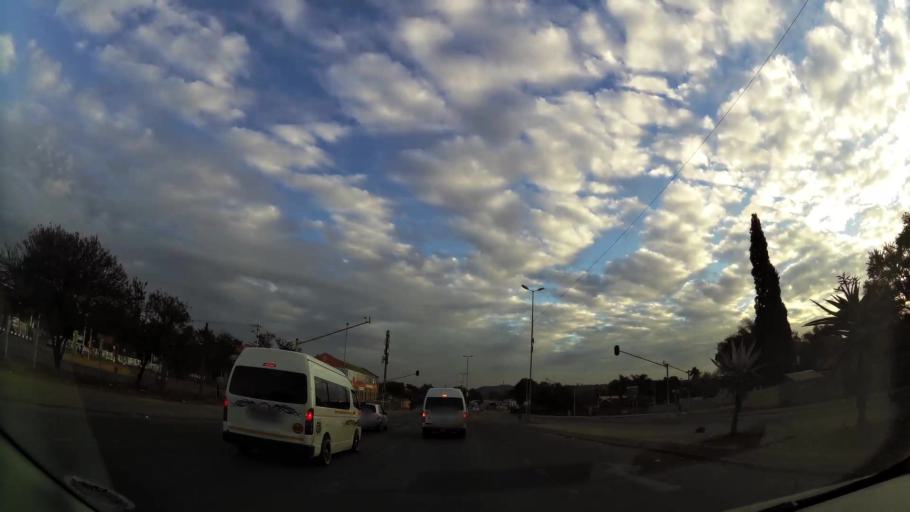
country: ZA
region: Gauteng
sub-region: City of Tshwane Metropolitan Municipality
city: Pretoria
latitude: -25.7324
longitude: 28.3165
